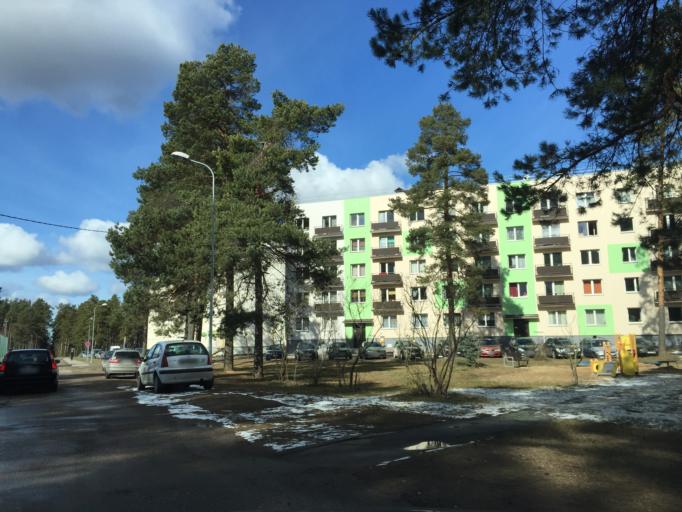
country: LV
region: Garkalne
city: Garkalne
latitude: 56.9641
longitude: 24.4290
